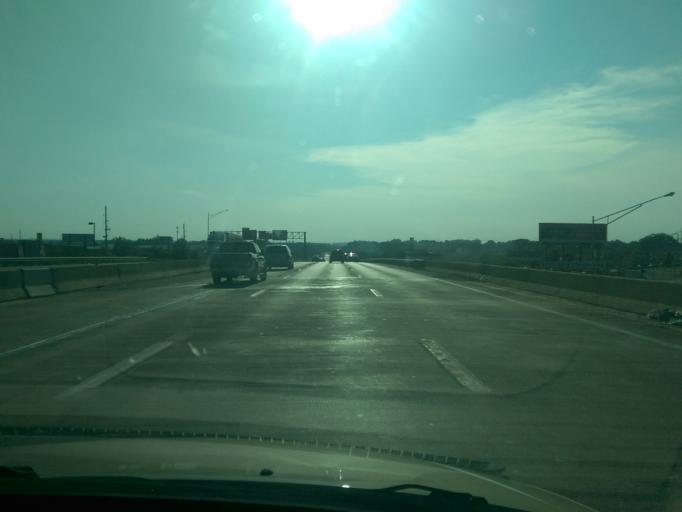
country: US
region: Missouri
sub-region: Jackson County
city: Raytown
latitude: 39.0473
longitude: -94.4432
